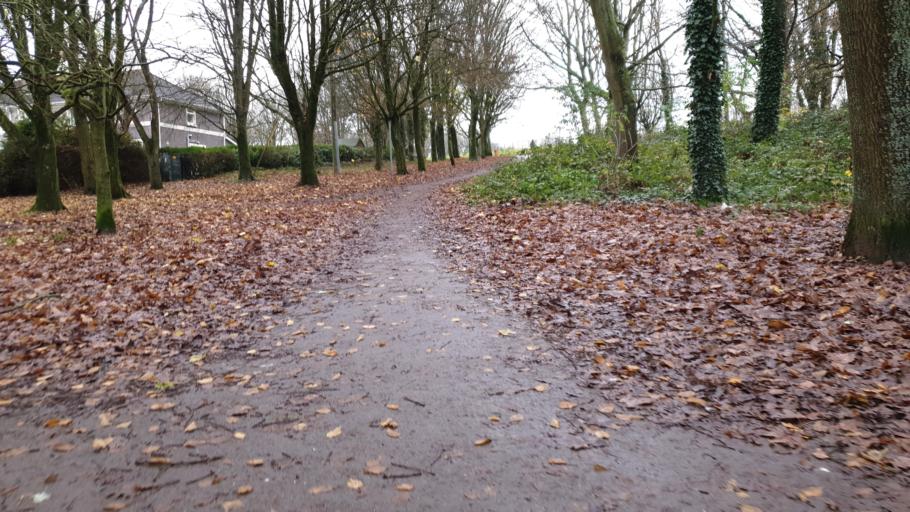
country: IE
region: Munster
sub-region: County Cork
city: Cork
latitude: 51.8919
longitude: -8.4289
